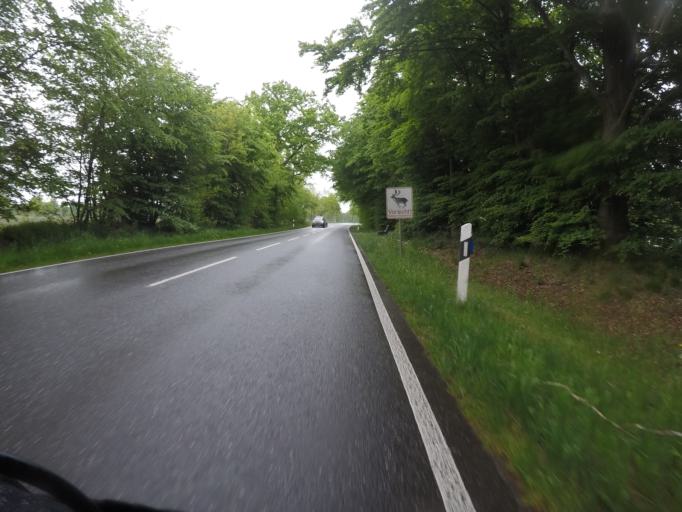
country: DE
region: Schleswig-Holstein
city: Heidmuhlen
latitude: 53.9564
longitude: 10.0857
